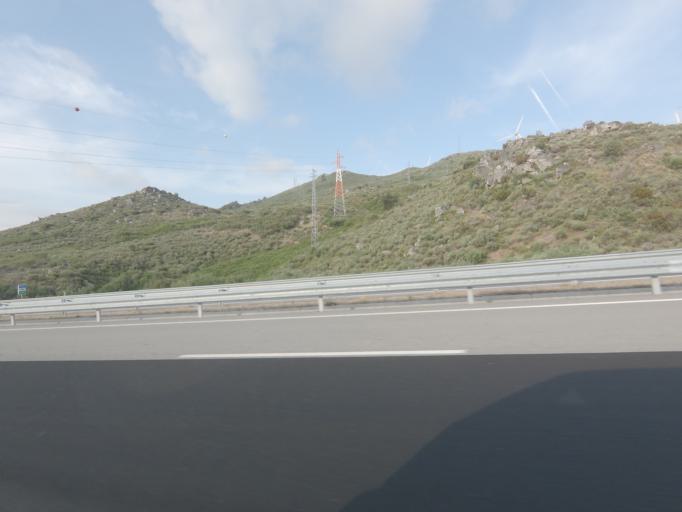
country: PT
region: Vila Real
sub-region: Vila Pouca de Aguiar
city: Vila Pouca de Aguiar
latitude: 41.4644
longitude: -7.6447
